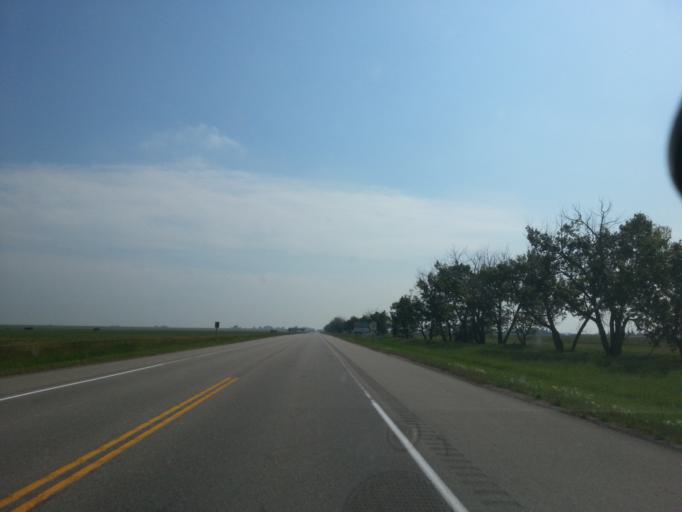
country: CA
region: Alberta
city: Irricana
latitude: 51.3869
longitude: -113.5162
